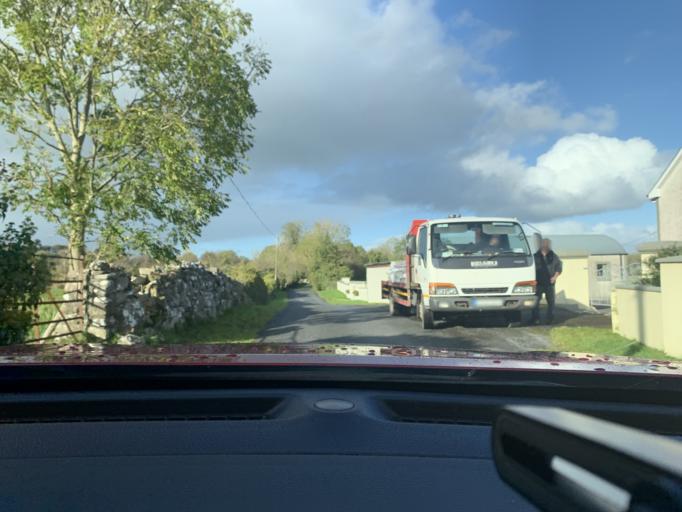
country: IE
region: Connaught
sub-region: Sligo
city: Ballymote
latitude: 54.1053
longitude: -8.4340
